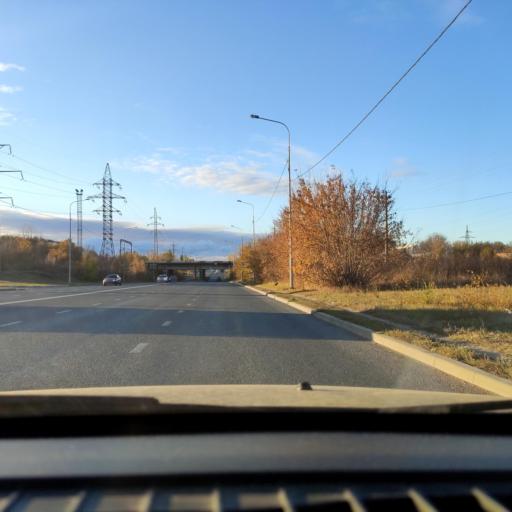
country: RU
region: Samara
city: Tol'yatti
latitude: 53.5688
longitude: 49.2913
